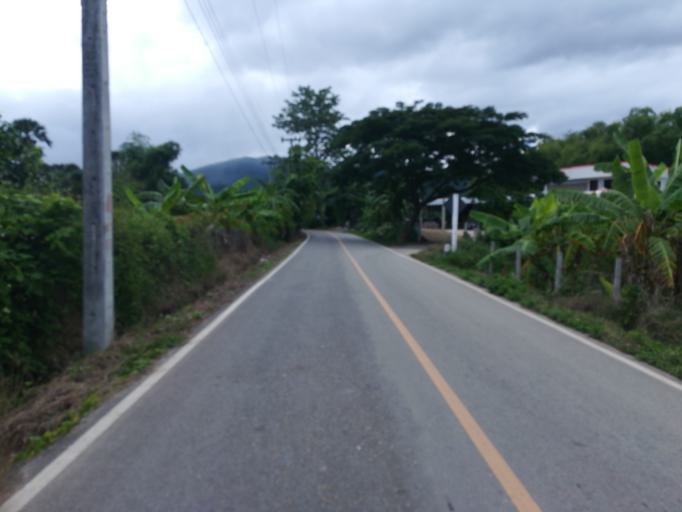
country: TH
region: Chiang Mai
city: Chom Thong
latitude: 18.4124
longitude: 98.6623
